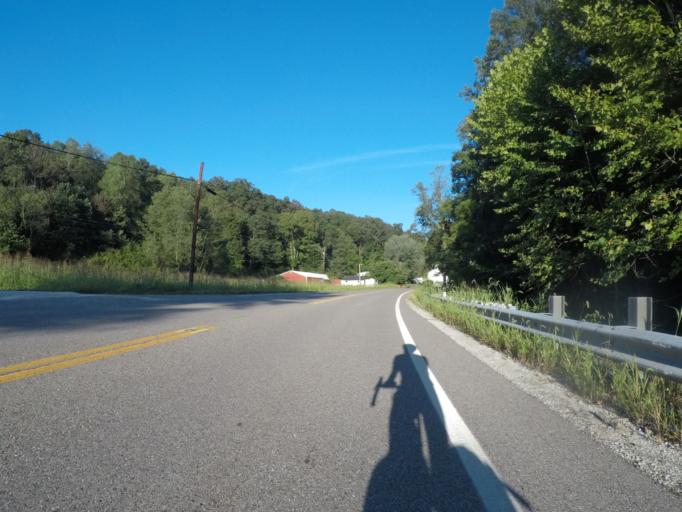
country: US
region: Ohio
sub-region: Lawrence County
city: Coal Grove
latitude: 38.5737
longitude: -82.5454
